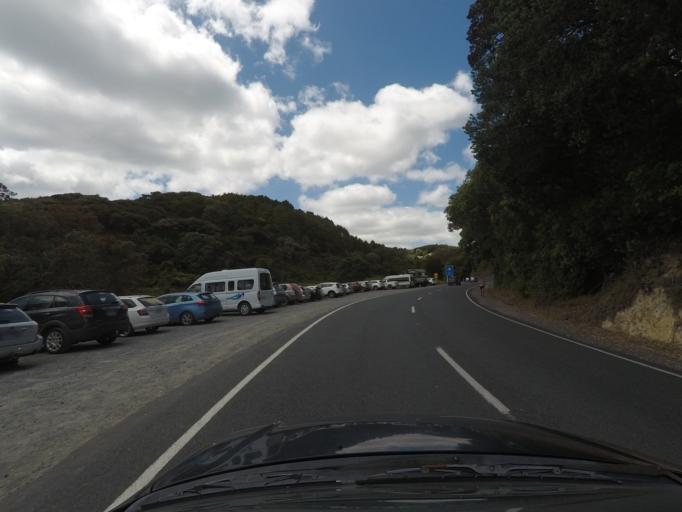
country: NZ
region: Northland
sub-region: Whangarei
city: Ruakaka
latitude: -36.0307
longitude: 174.5088
